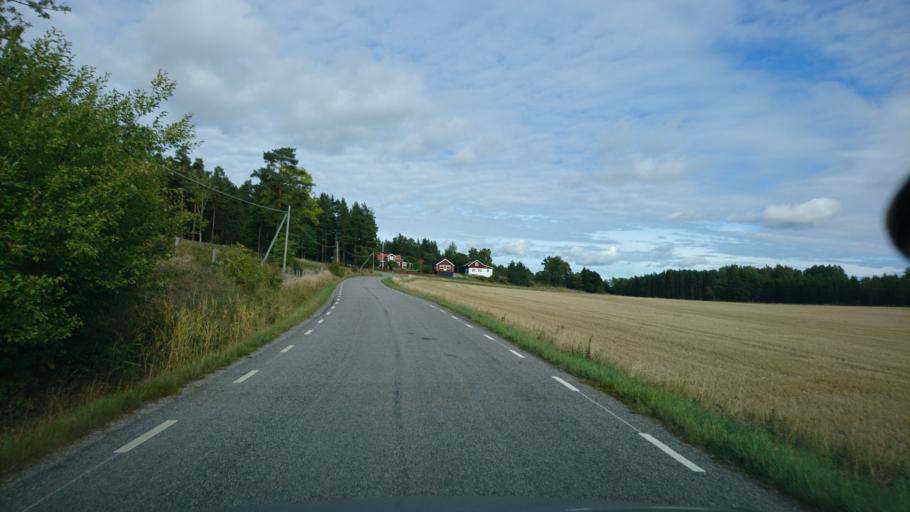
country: SE
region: Soedermanland
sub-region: Strangnas Kommun
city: Stallarholmen
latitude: 59.3879
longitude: 17.2657
